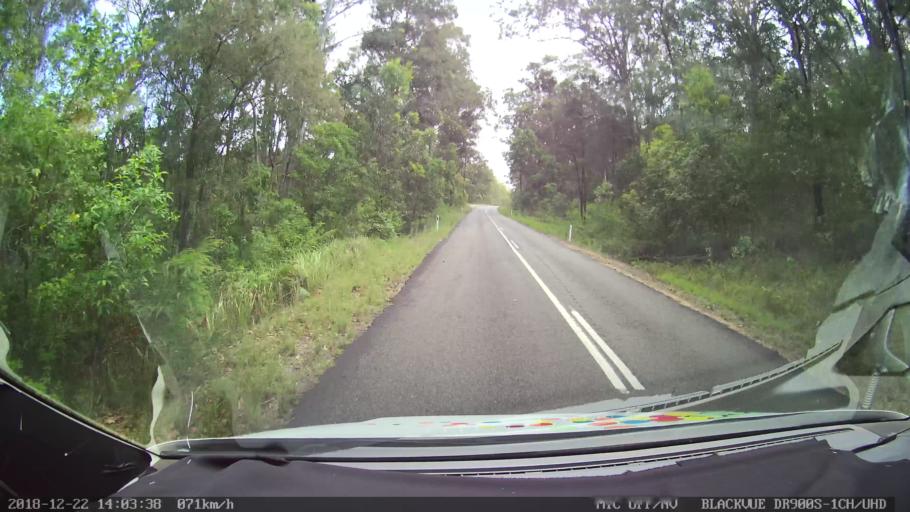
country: AU
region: New South Wales
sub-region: Clarence Valley
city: Coutts Crossing
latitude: -29.9307
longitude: 152.7363
